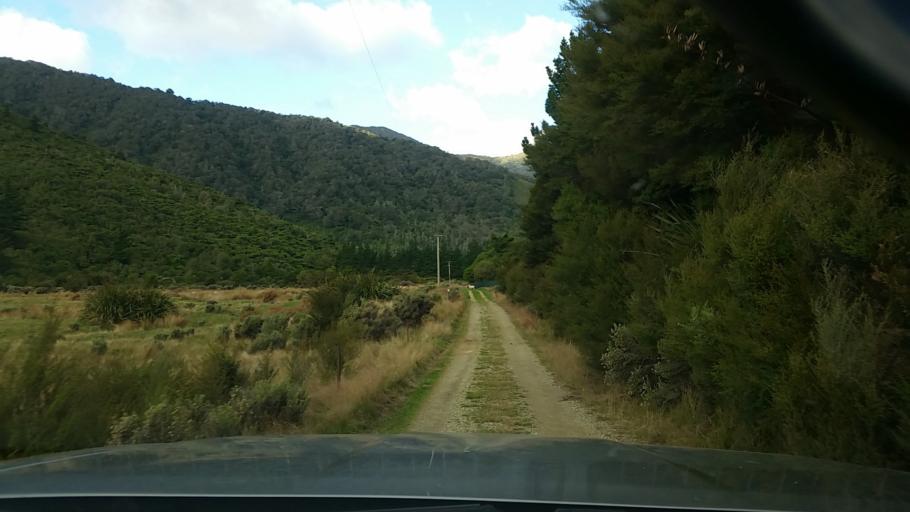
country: NZ
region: Marlborough
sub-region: Marlborough District
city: Picton
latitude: -41.0626
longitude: 174.1189
